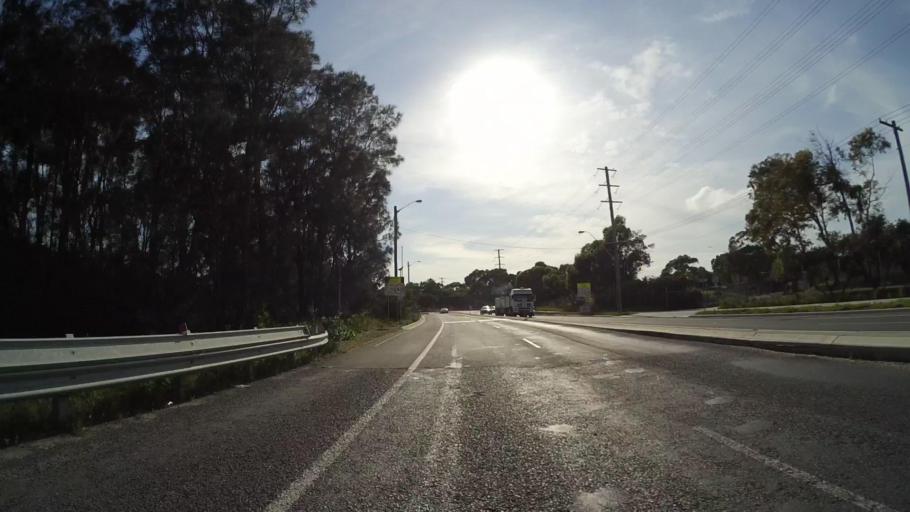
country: AU
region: New South Wales
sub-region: Sutherland Shire
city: Cronulla
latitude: -34.0395
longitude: 151.1550
